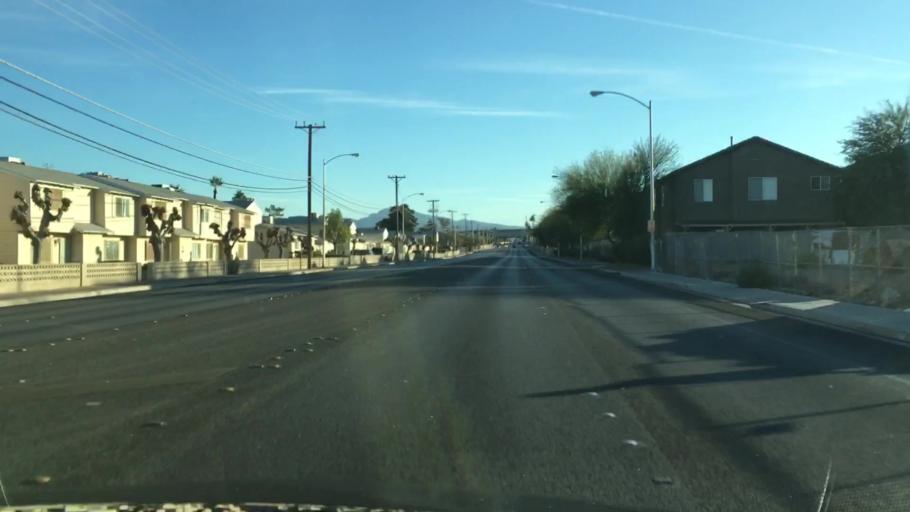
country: US
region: Nevada
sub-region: Clark County
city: Whitney
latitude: 36.0989
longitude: -115.0733
